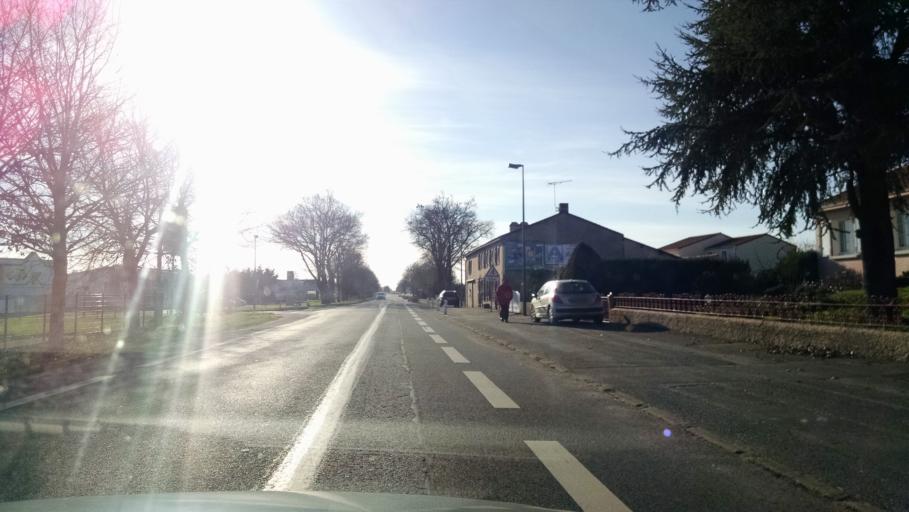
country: FR
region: Pays de la Loire
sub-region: Departement de la Vendee
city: Montaigu
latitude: 46.9736
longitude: -1.3242
